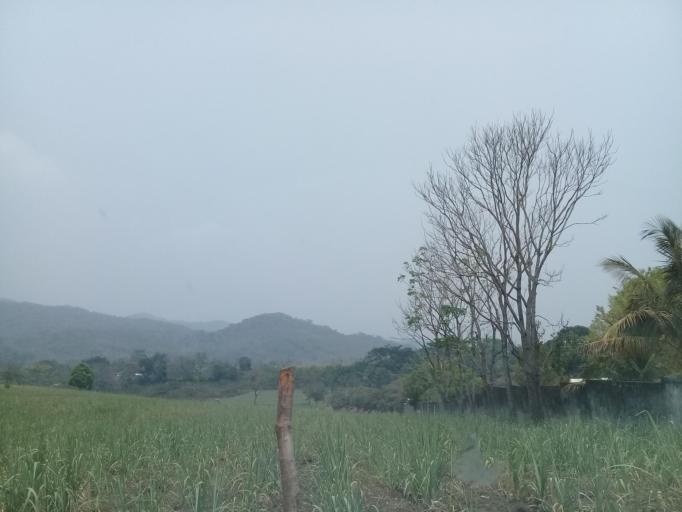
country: MX
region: Veracruz
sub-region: Tezonapa
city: Laguna Chica (Pueblo Nuevo)
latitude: 18.5379
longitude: -96.7390
